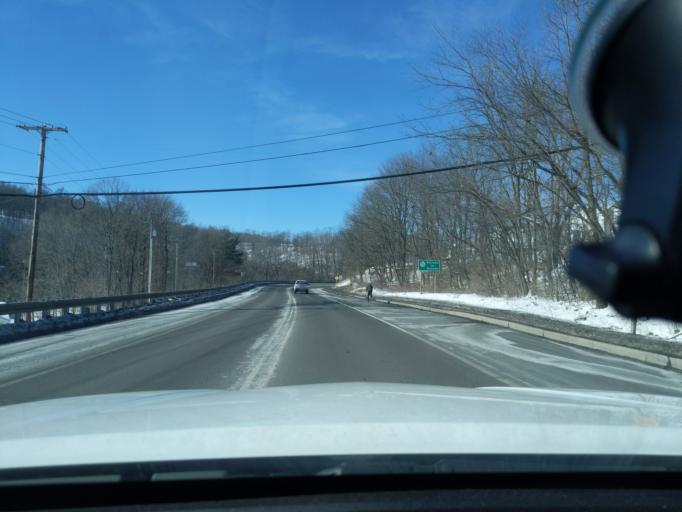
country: US
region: Maryland
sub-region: Allegany County
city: Lonaconing
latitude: 39.5873
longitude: -78.9499
